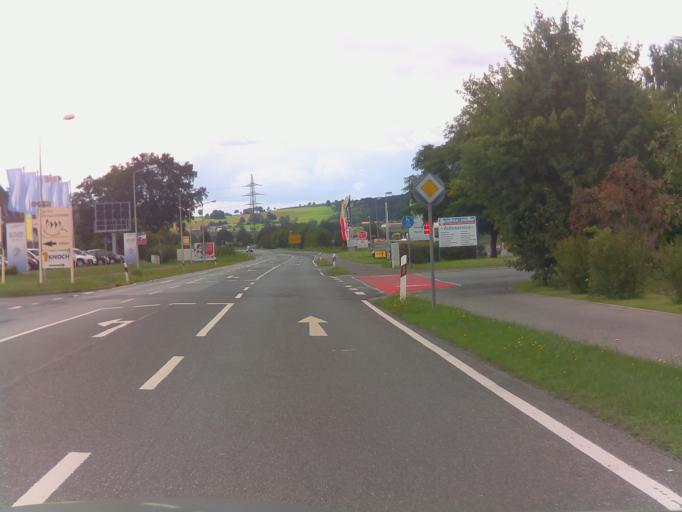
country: DE
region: Bavaria
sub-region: Upper Franconia
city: Neustadt bei Coburg
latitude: 50.3138
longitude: 11.1138
